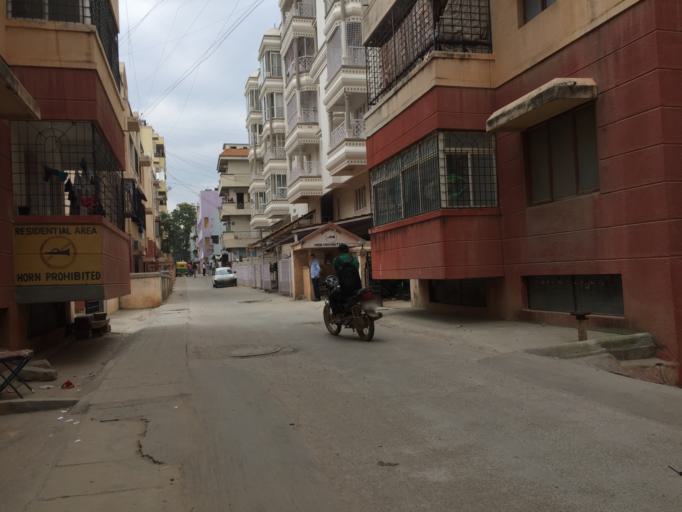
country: IN
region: Karnataka
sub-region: Bangalore Urban
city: Bangalore
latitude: 12.9566
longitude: 77.6593
